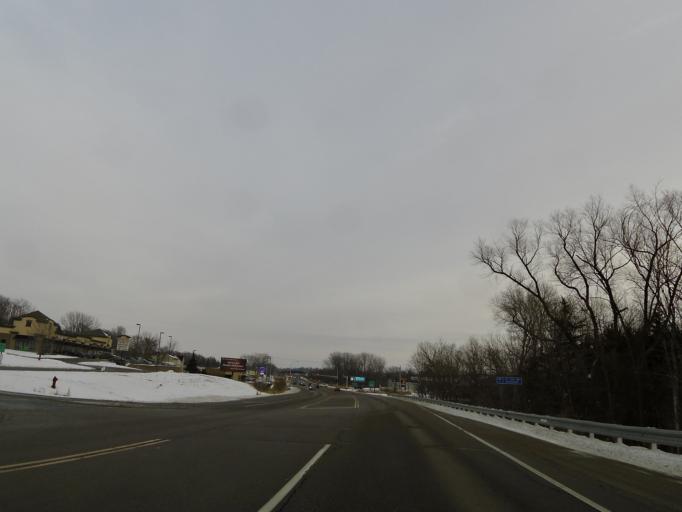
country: US
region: Minnesota
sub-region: Hennepin County
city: Saint Bonifacius
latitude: 44.9020
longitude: -93.7508
